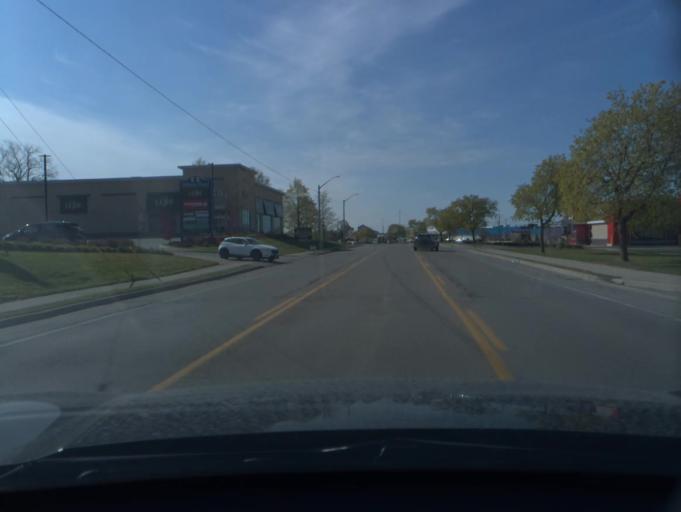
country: CA
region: Ontario
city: North Perth
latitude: 43.8376
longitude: -80.9999
